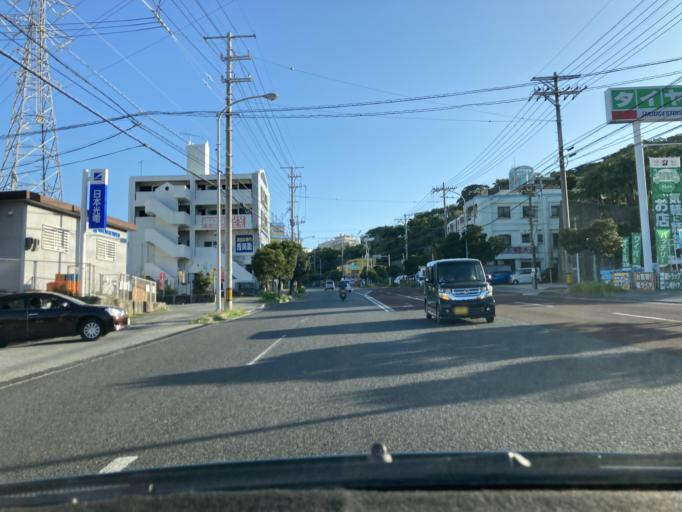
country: JP
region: Okinawa
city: Ginowan
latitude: 26.2465
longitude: 127.7375
